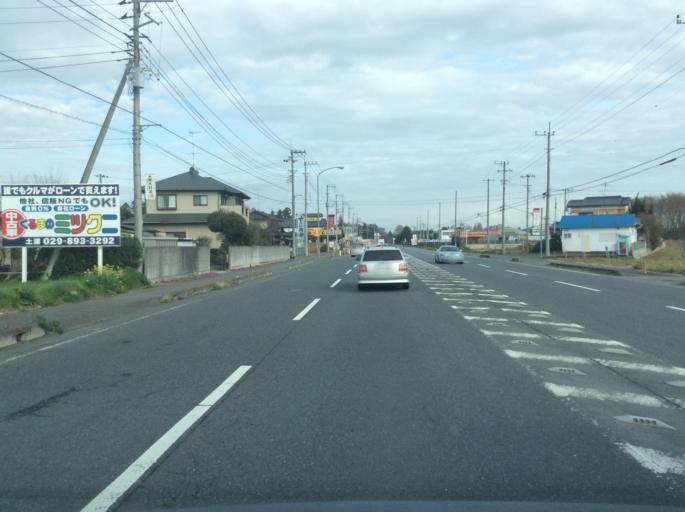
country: JP
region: Ibaraki
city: Tsukuba
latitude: 36.1901
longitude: 140.0182
